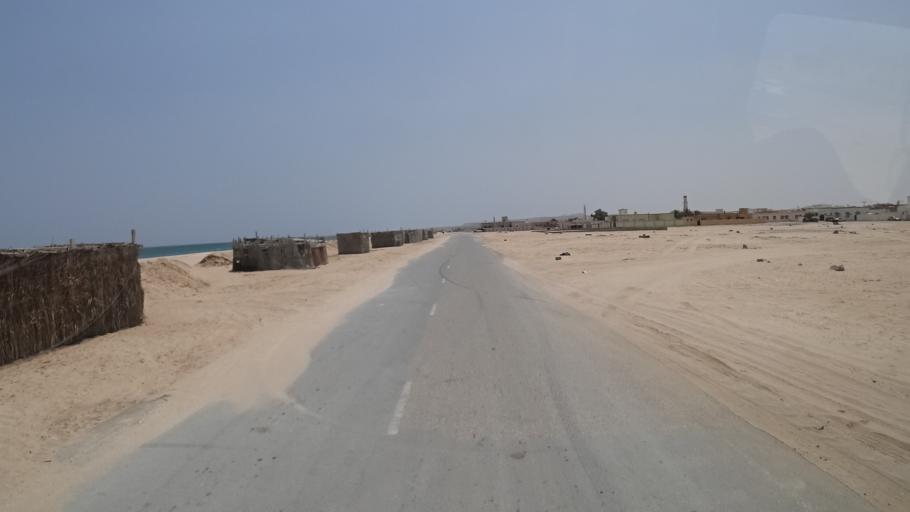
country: OM
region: Ash Sharqiyah
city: Sur
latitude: 22.5233
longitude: 59.7983
